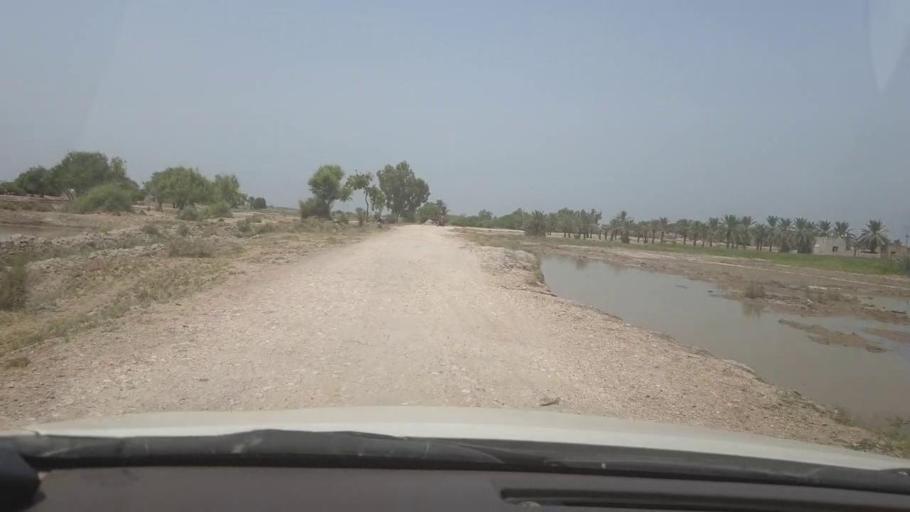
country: PK
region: Sindh
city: Shikarpur
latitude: 27.9446
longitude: 68.5718
